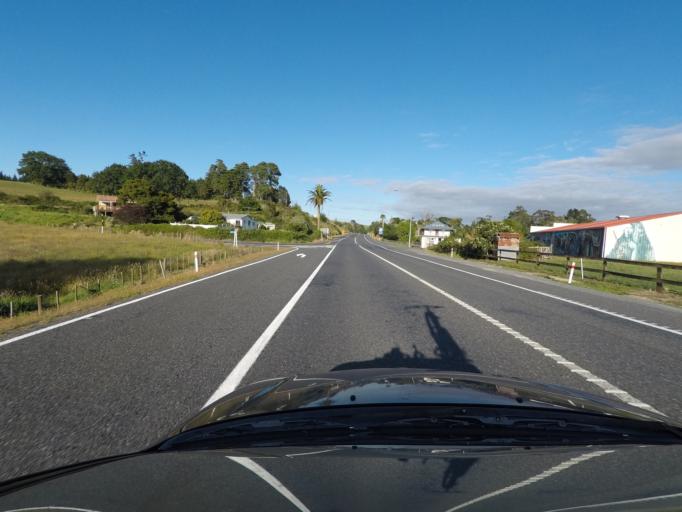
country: NZ
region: Northland
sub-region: Far North District
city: Kawakawa
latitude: -35.5206
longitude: 174.2039
